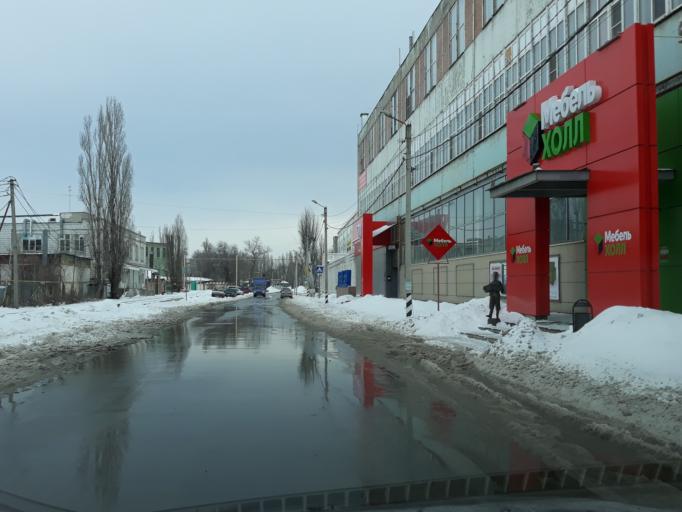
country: RU
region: Rostov
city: Taganrog
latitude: 47.2159
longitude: 38.9343
